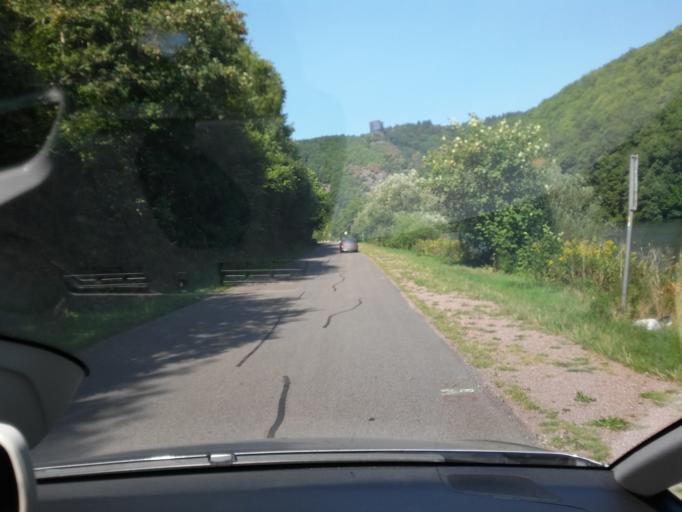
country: DE
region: Saarland
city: Orscholz
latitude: 49.4938
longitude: 6.5538
